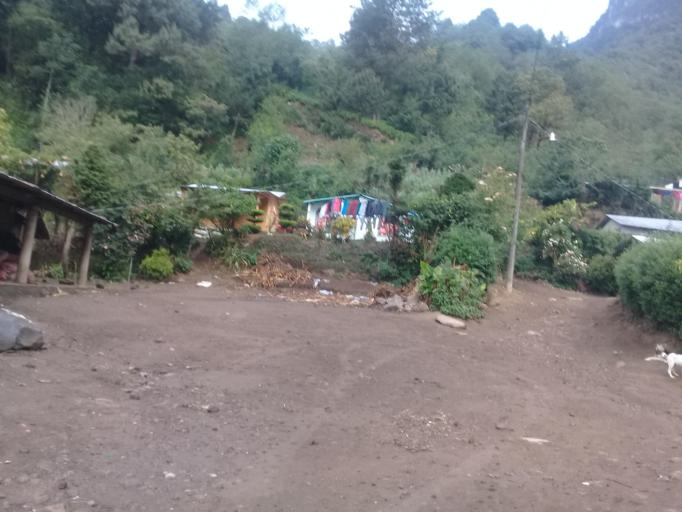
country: MX
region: Veracruz
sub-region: Mariano Escobedo
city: San Isidro el Berro
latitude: 18.9588
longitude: -97.1967
